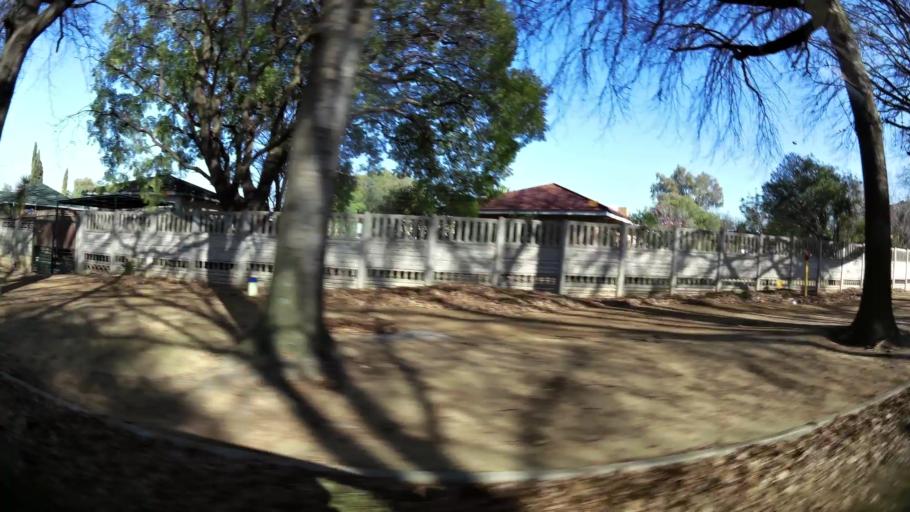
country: ZA
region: Gauteng
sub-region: Ekurhuleni Metropolitan Municipality
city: Benoni
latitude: -26.1673
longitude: 28.3131
